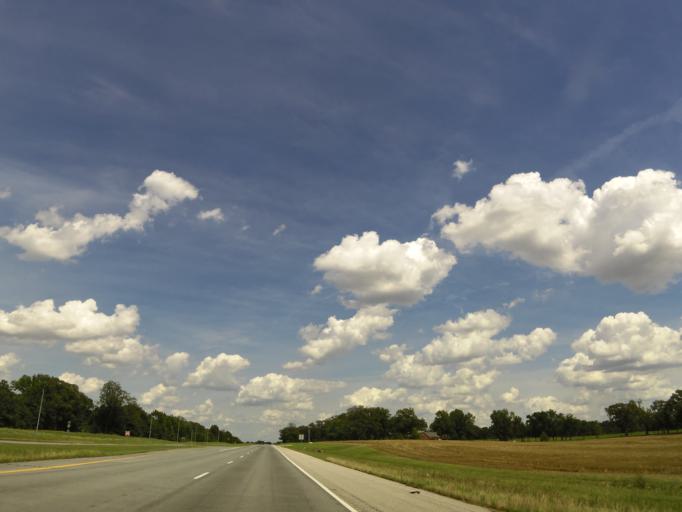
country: US
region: Tennessee
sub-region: Gibson County
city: Trenton
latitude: 35.9941
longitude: -89.0016
